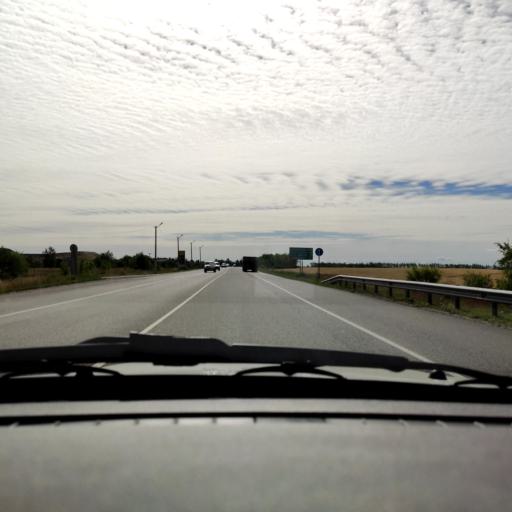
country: RU
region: Voronezj
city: Novaya Usman'
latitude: 51.6867
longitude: 39.4699
